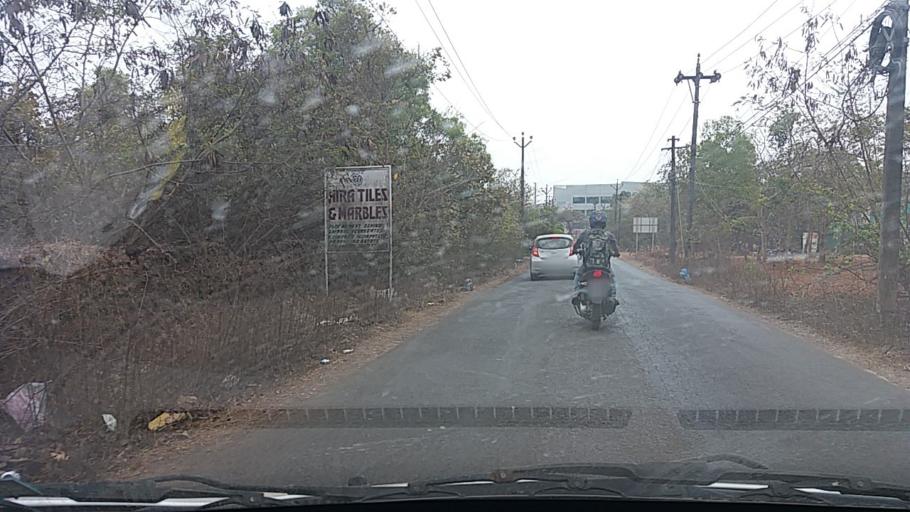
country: IN
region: Goa
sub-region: North Goa
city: Saligao
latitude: 15.5344
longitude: 73.7957
